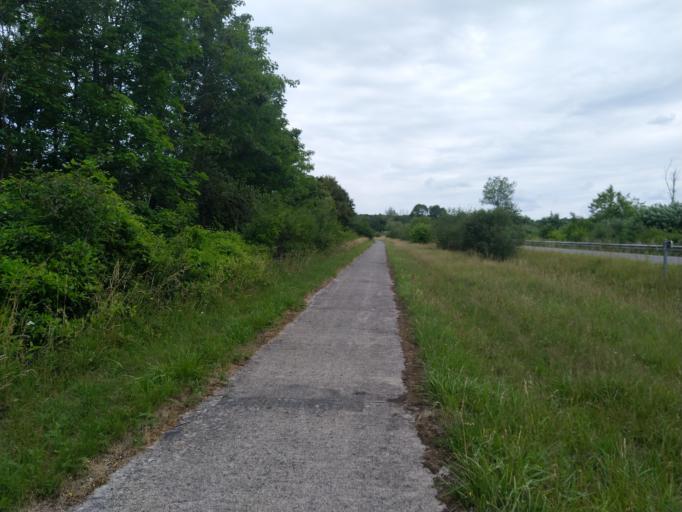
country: BE
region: Wallonia
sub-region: Province du Hainaut
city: Bernissart
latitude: 50.4889
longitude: 3.6443
